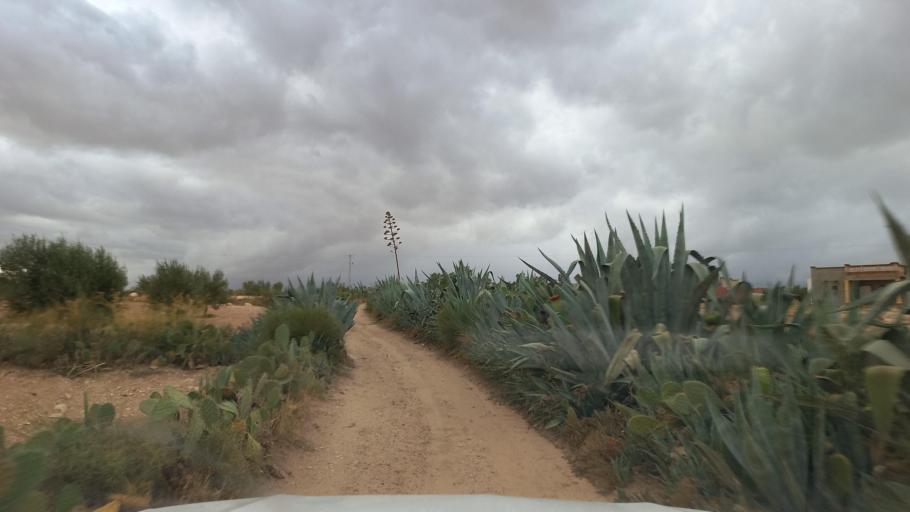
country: TN
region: Al Qasrayn
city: Kasserine
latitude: 35.2754
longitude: 8.9466
